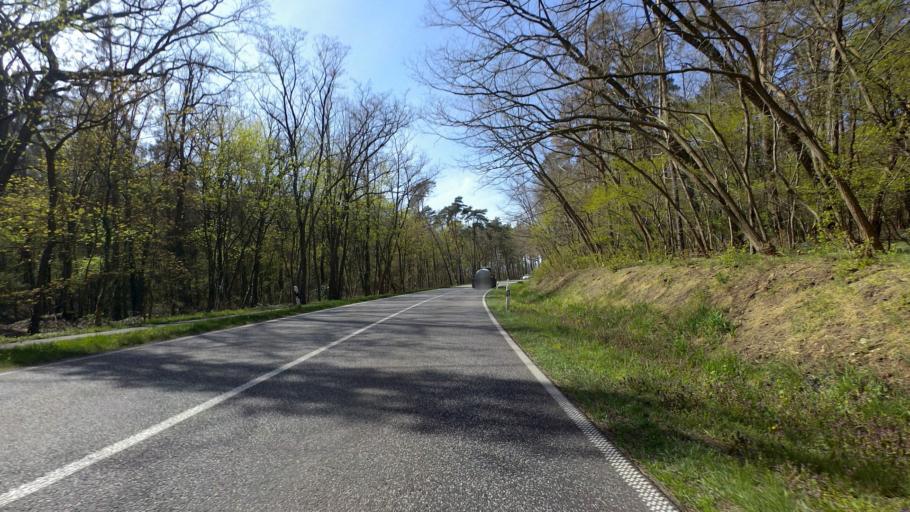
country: DE
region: Brandenburg
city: Trebbin
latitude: 52.2103
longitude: 13.1359
